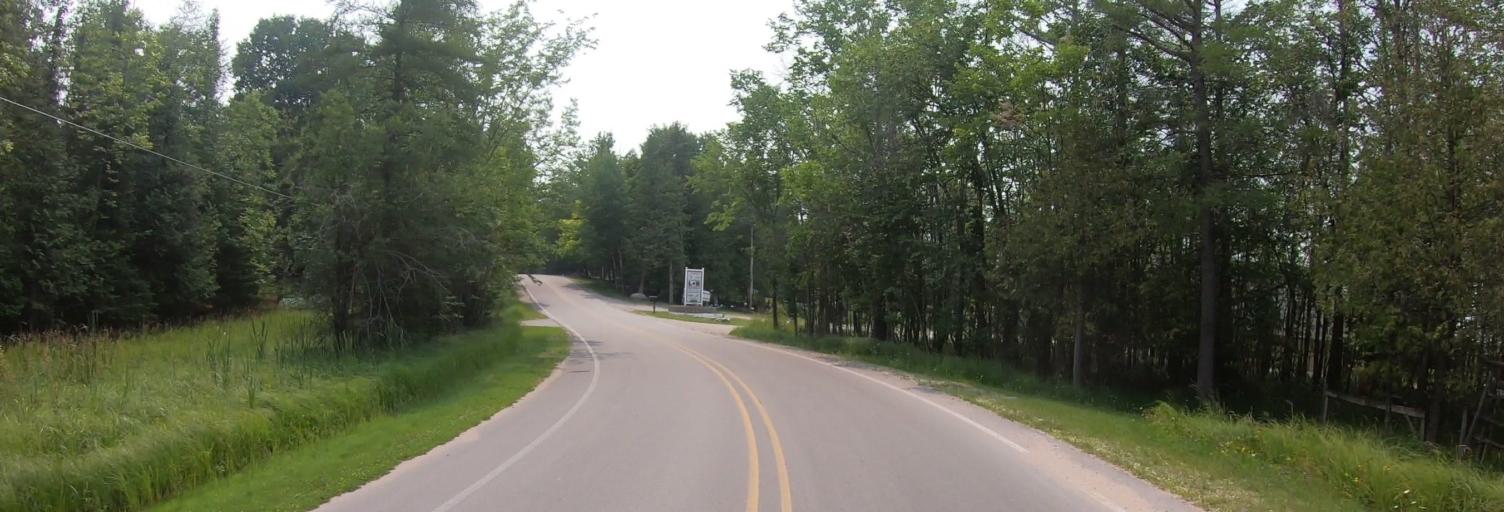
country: CA
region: Ontario
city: Thessalon
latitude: 46.0370
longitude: -83.7206
